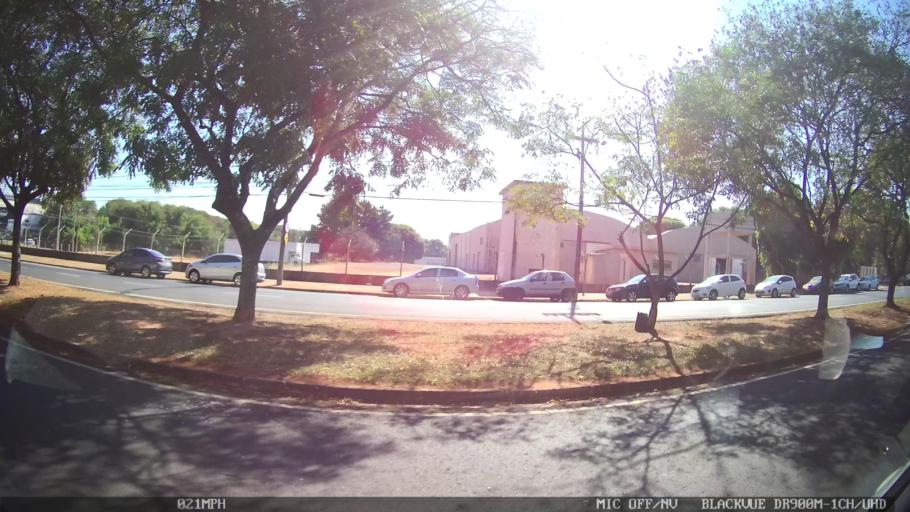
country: BR
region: Sao Paulo
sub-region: Sao Jose Do Rio Preto
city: Sao Jose do Rio Preto
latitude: -20.8108
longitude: -49.4143
